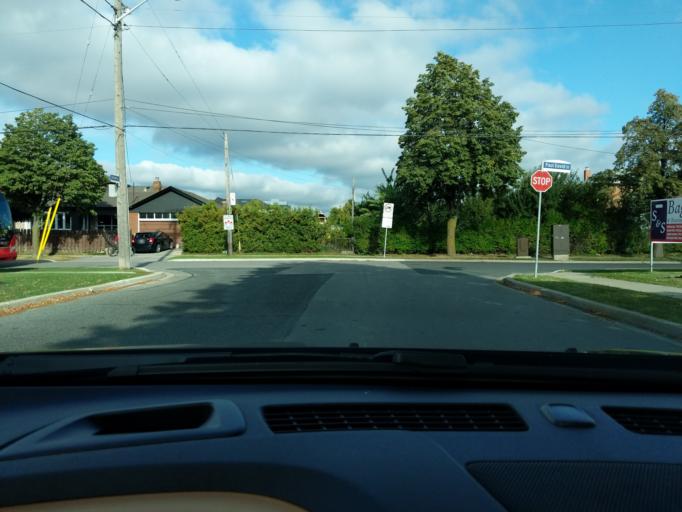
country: CA
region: Ontario
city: Toronto
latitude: 43.7209
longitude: -79.4628
